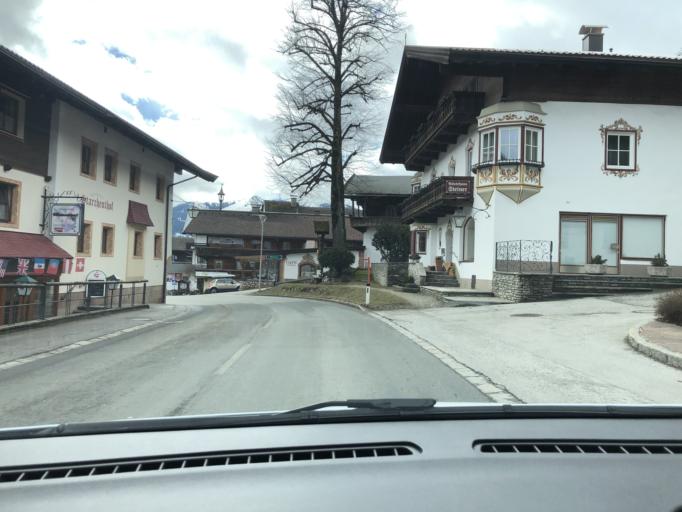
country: AT
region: Tyrol
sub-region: Politischer Bezirk Kufstein
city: Wildschoenau
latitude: 47.4444
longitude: 12.0489
